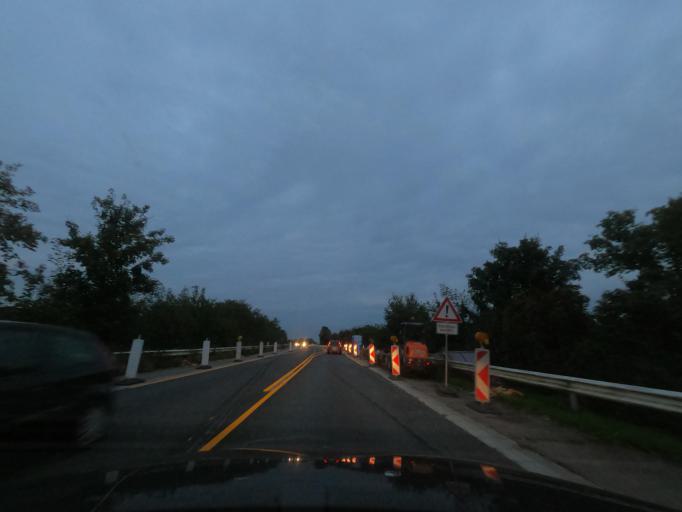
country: DE
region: North Rhine-Westphalia
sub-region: Regierungsbezirk Dusseldorf
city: Wesel
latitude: 51.6822
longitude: 6.6064
